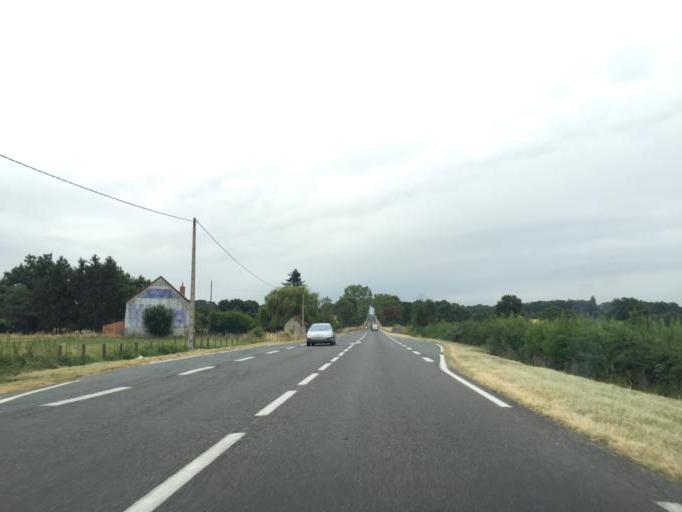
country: FR
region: Auvergne
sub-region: Departement de l'Allier
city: Brout-Vernet
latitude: 46.2045
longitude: 3.2776
